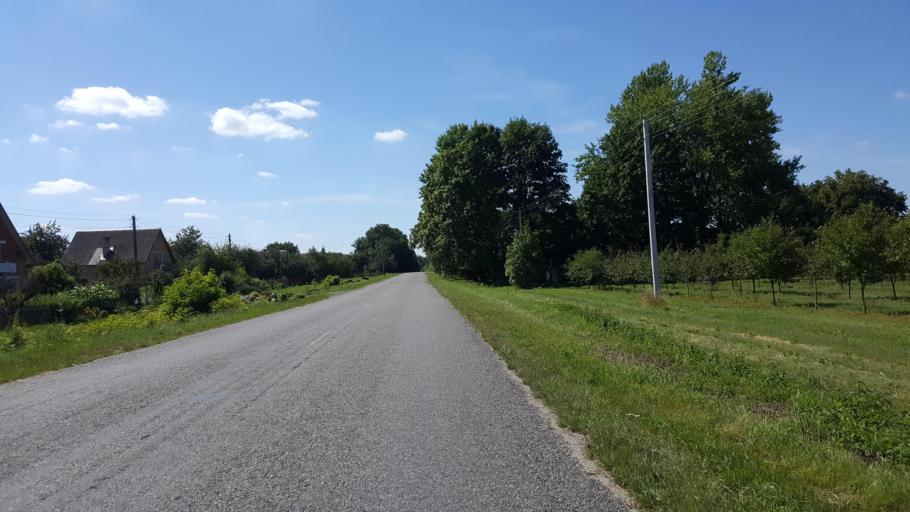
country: BY
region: Brest
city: Charnawchytsy
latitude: 52.3625
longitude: 23.6233
